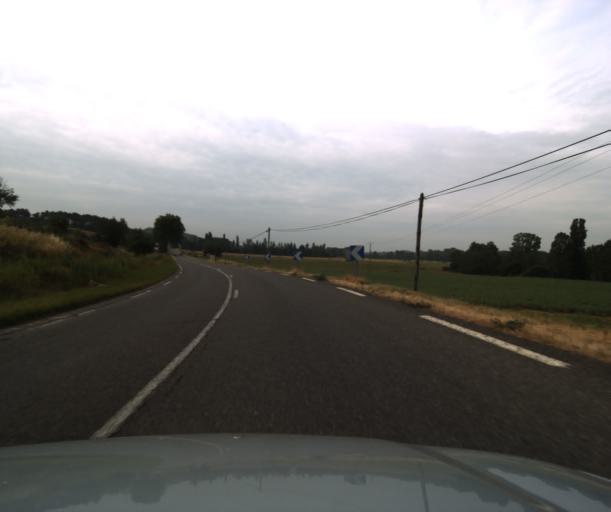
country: FR
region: Midi-Pyrenees
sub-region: Departement du Gers
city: Mirande
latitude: 43.5290
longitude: 0.4162
